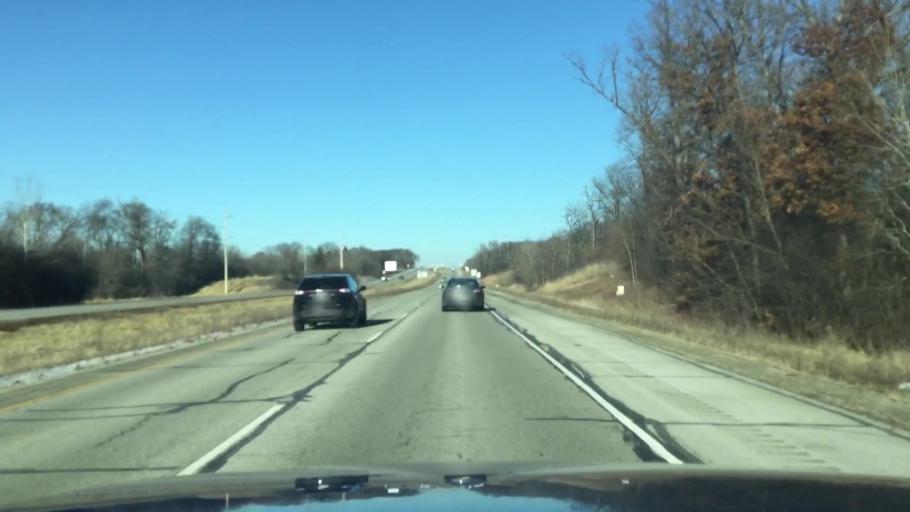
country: US
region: Wisconsin
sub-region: Racine County
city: Rochester
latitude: 42.7303
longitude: -88.2201
